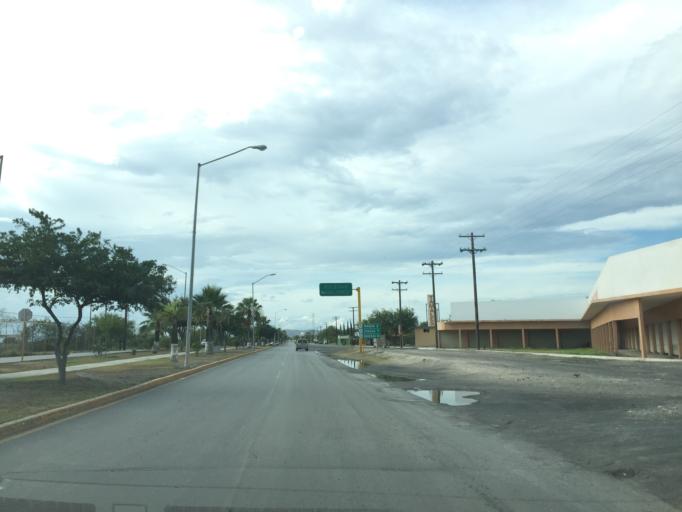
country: MX
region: Nuevo Leon
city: Marin
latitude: 25.8565
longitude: -100.0233
